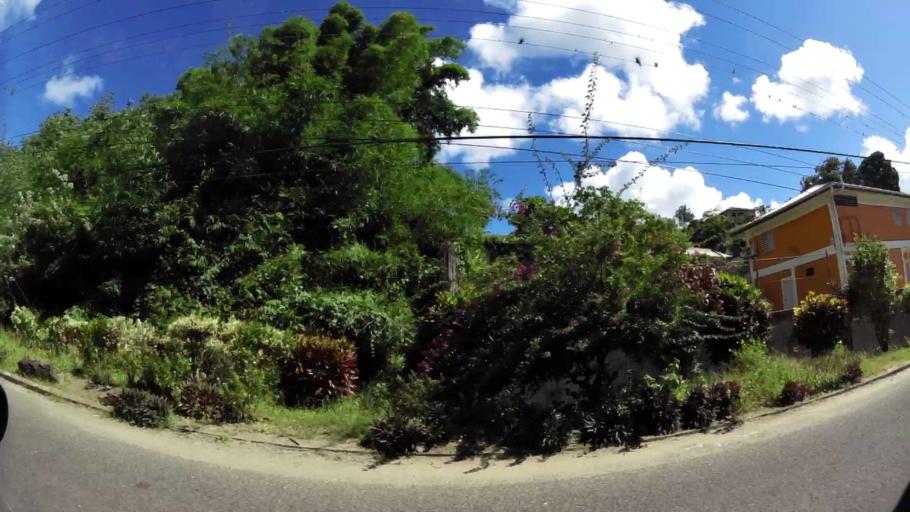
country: TT
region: Tobago
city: Scarborough
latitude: 11.2284
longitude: -60.7412
